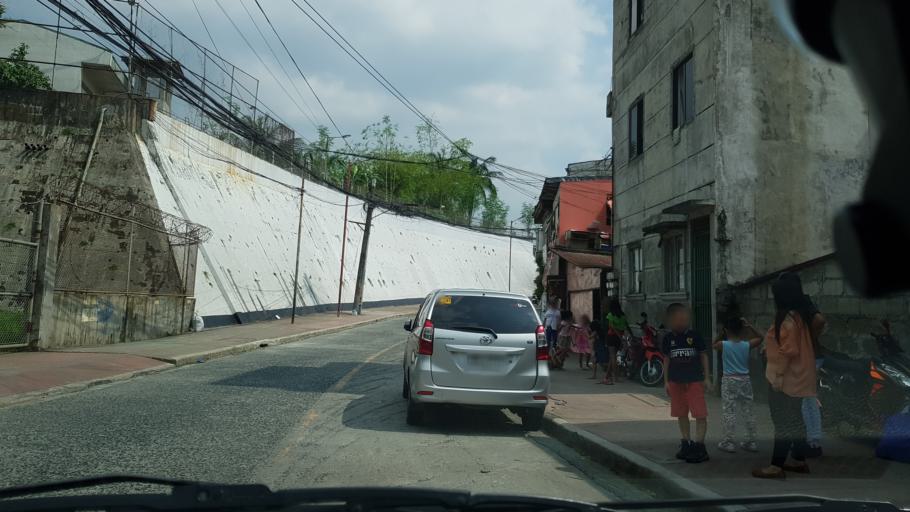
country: PH
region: Calabarzon
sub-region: Province of Rizal
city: Antipolo
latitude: 14.6613
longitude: 121.1278
